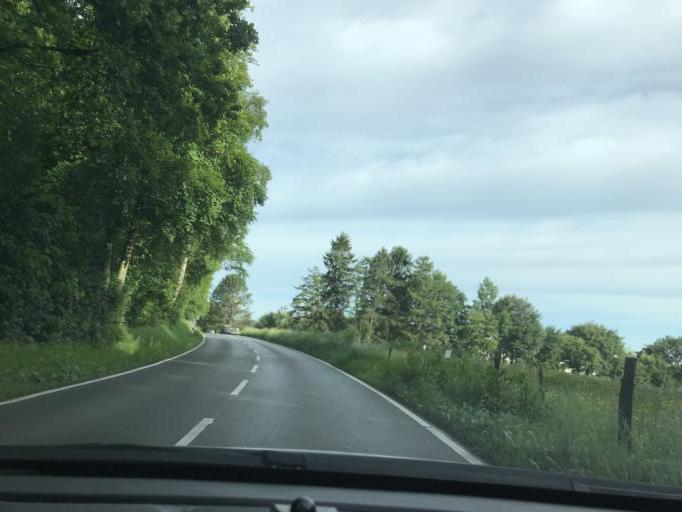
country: DE
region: North Rhine-Westphalia
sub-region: Regierungsbezirk Koln
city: Aachen
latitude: 50.7500
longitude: 6.1128
